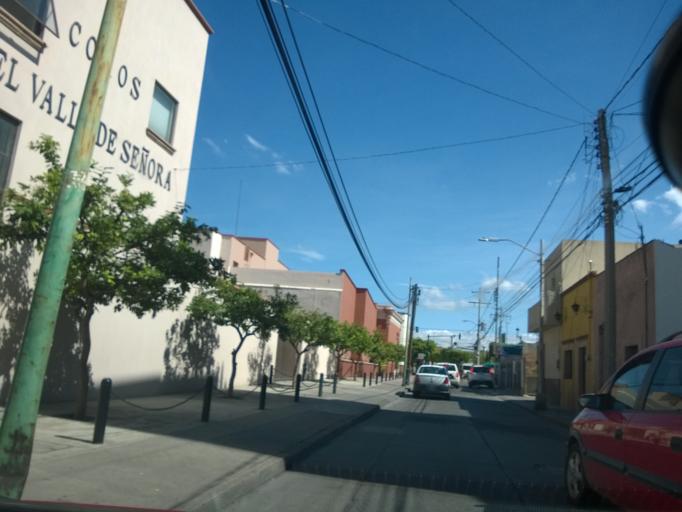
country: MX
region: Guanajuato
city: Leon
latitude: 21.1196
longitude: -101.6762
